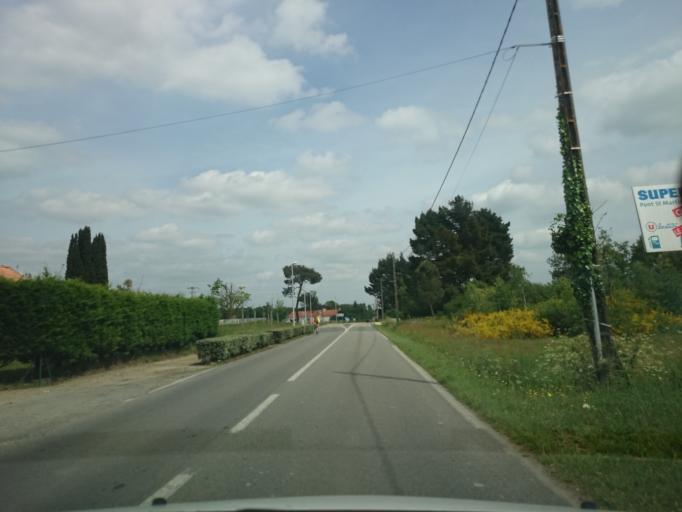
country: FR
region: Pays de la Loire
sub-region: Departement de la Loire-Atlantique
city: Pont-Saint-Martin
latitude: 47.1252
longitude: -1.6100
